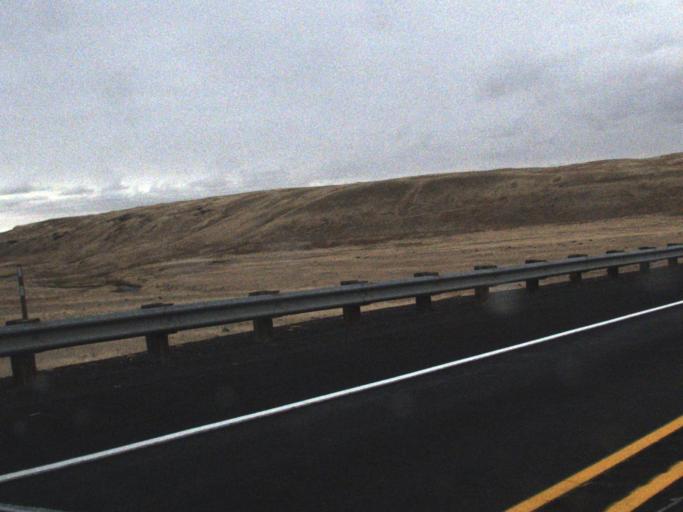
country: US
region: Washington
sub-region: Adams County
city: Ritzville
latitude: 46.7700
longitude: -118.1451
